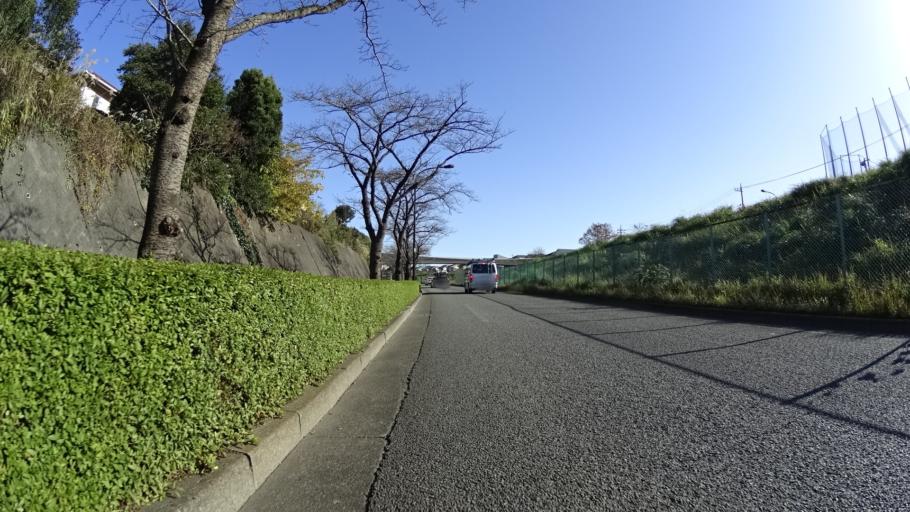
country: JP
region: Tokyo
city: Hino
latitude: 35.6095
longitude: 139.4219
